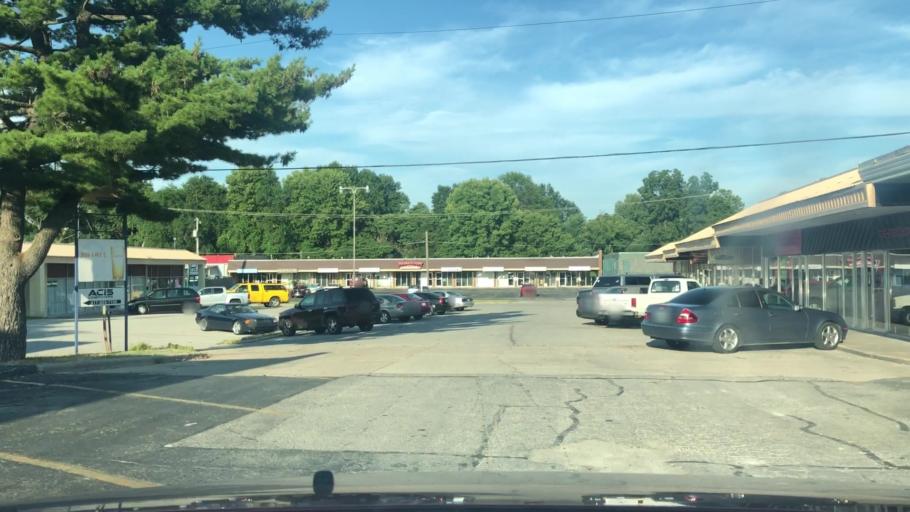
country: US
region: Missouri
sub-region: Greene County
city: Springfield
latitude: 37.1782
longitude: -93.2612
